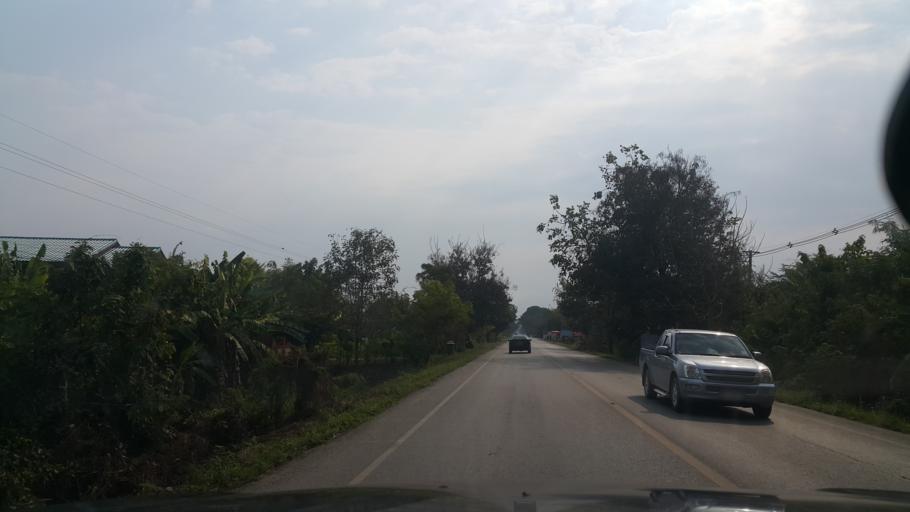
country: TH
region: Sukhothai
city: Si Samrong
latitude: 17.1805
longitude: 99.8382
